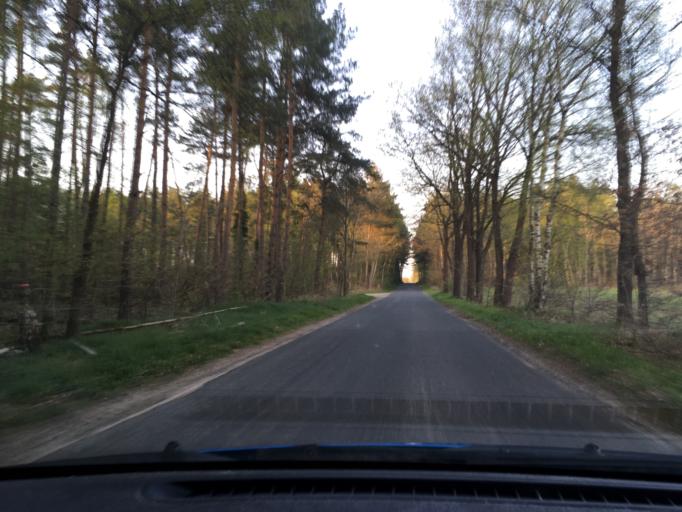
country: DE
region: Lower Saxony
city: Oldendorf
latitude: 53.1795
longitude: 10.2601
